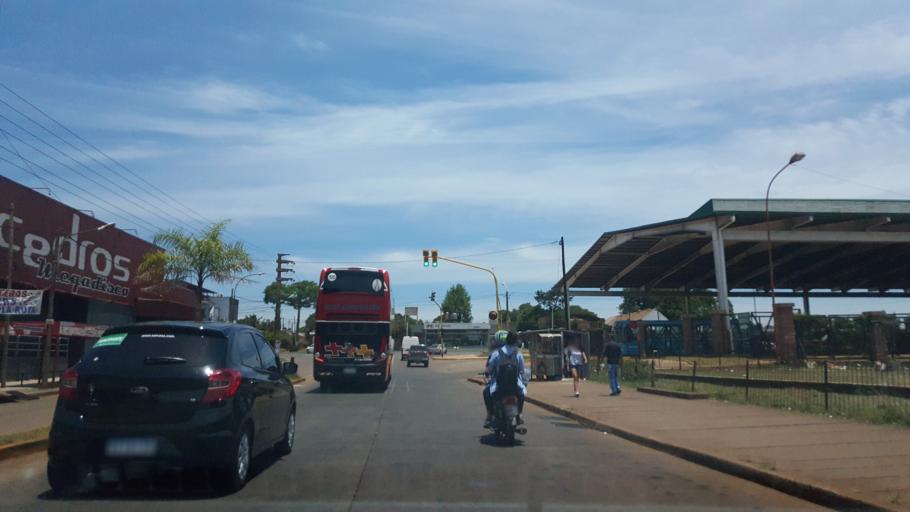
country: AR
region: Misiones
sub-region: Departamento de Capital
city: Posadas
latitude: -27.4022
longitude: -55.9138
